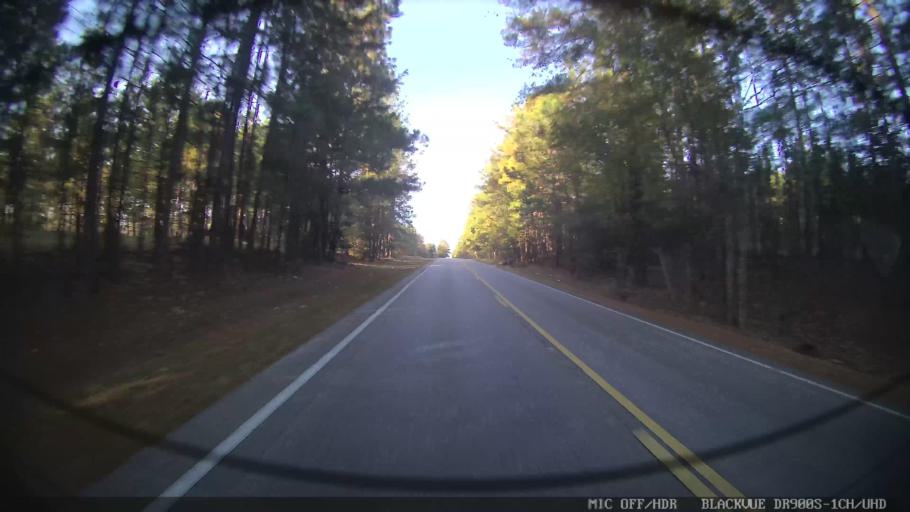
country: US
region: Mississippi
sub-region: Lamar County
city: Purvis
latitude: 31.0913
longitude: -89.4154
